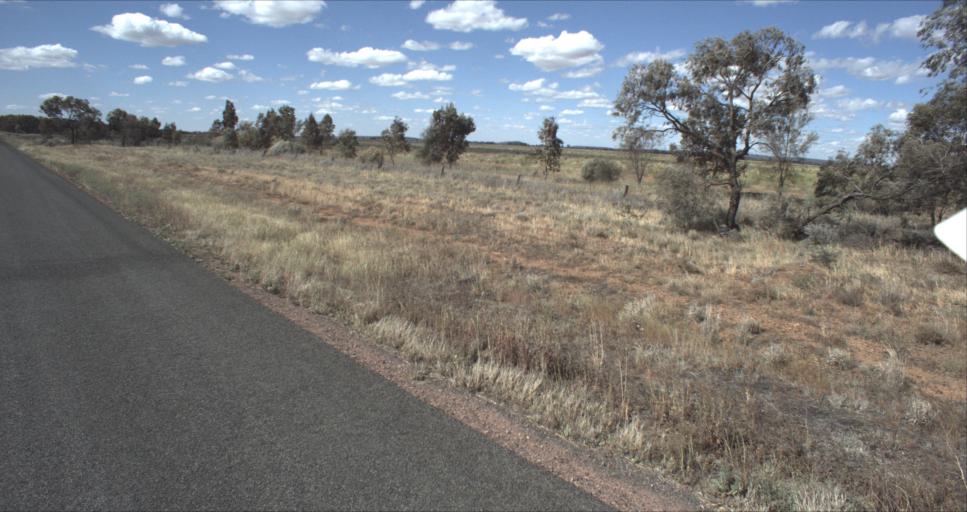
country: AU
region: New South Wales
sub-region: Leeton
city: Leeton
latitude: -34.4349
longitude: 146.2575
